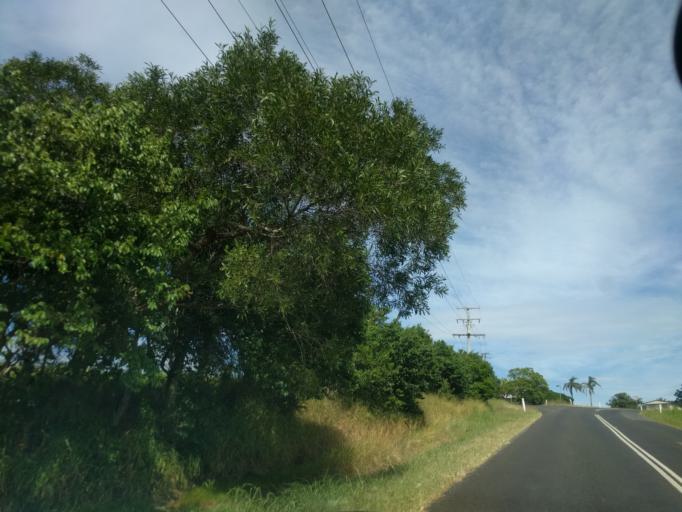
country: AU
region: Queensland
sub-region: Ipswich
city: Thagoona
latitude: -27.5983
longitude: 152.5699
